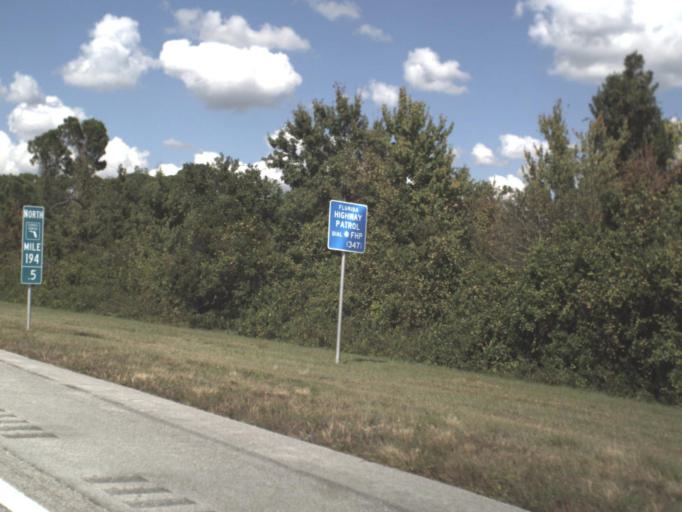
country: US
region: Florida
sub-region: Indian River County
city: Fellsmere
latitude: 27.7146
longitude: -80.8986
